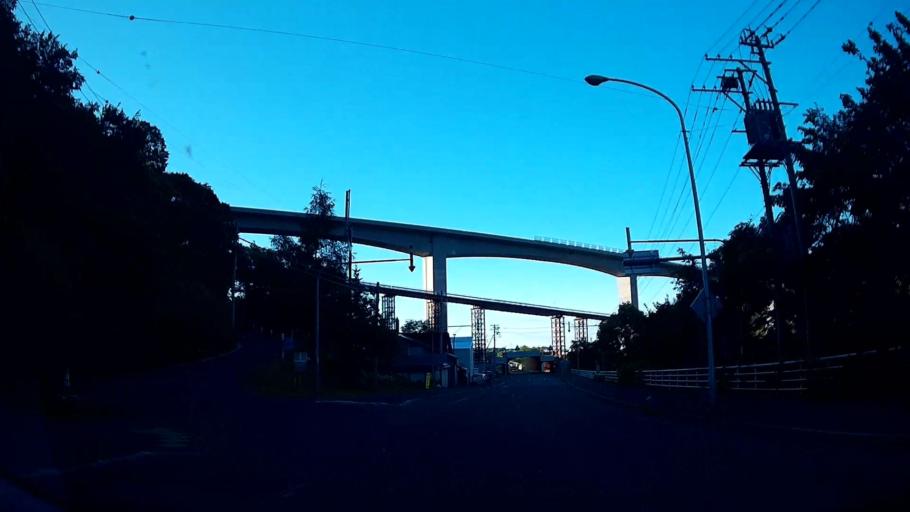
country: JP
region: Hokkaido
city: Otaru
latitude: 43.1512
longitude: 141.0409
